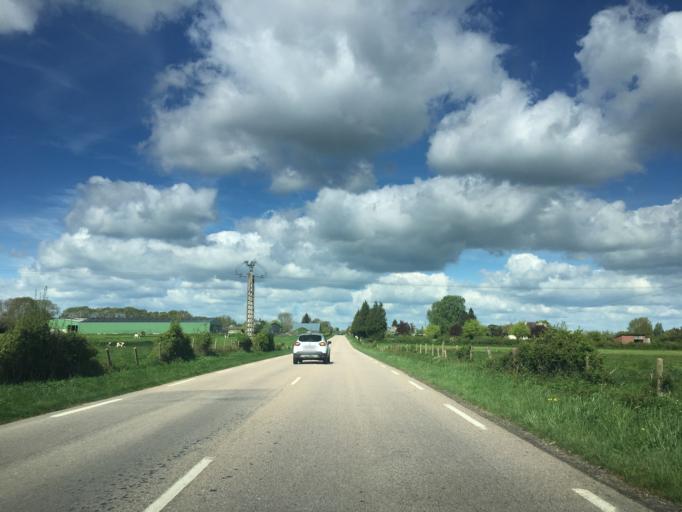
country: FR
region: Lower Normandy
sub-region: Departement de l'Orne
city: Aube-sur-Rile
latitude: 48.8351
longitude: 0.5341
